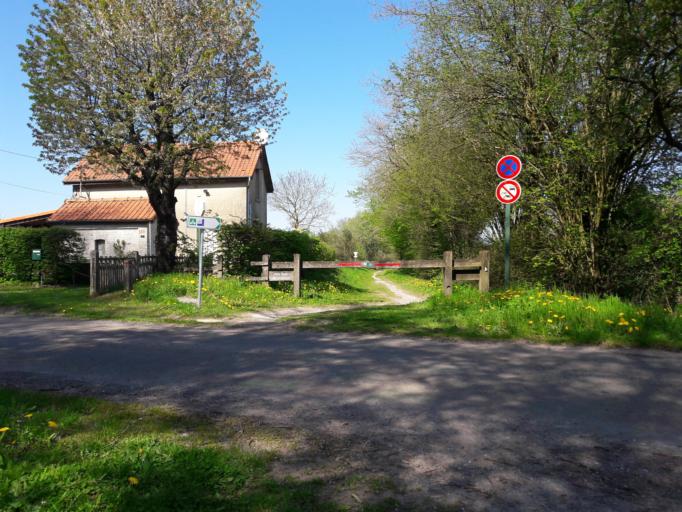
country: FR
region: Nord-Pas-de-Calais
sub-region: Departement du Nord
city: Sains-du-Nord
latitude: 50.1622
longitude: 4.0715
